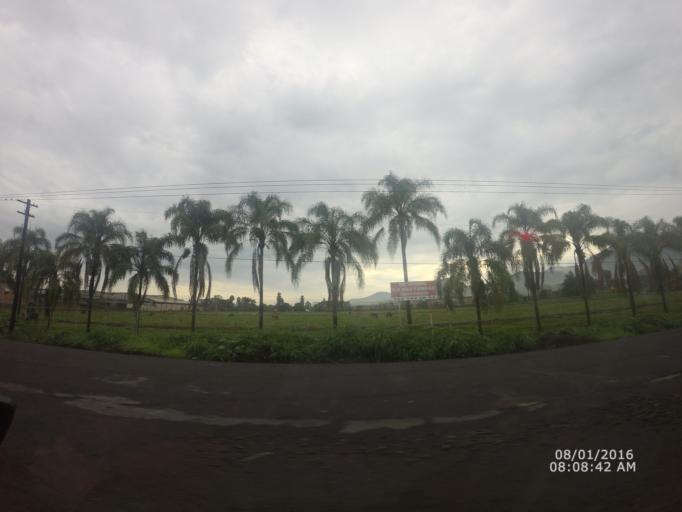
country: MX
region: Nayarit
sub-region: Tepic
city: La Corregidora
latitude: 21.4554
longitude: -104.8220
